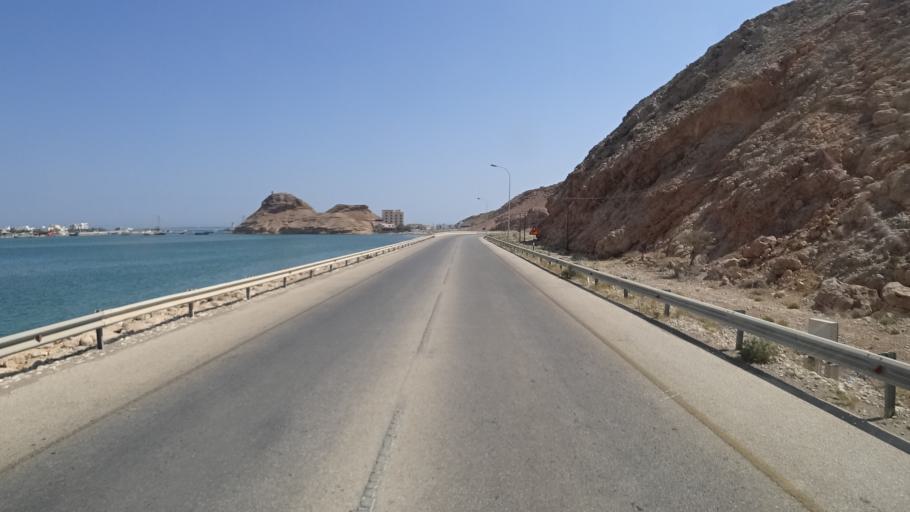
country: OM
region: Ash Sharqiyah
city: Sur
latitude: 22.5552
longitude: 59.5386
